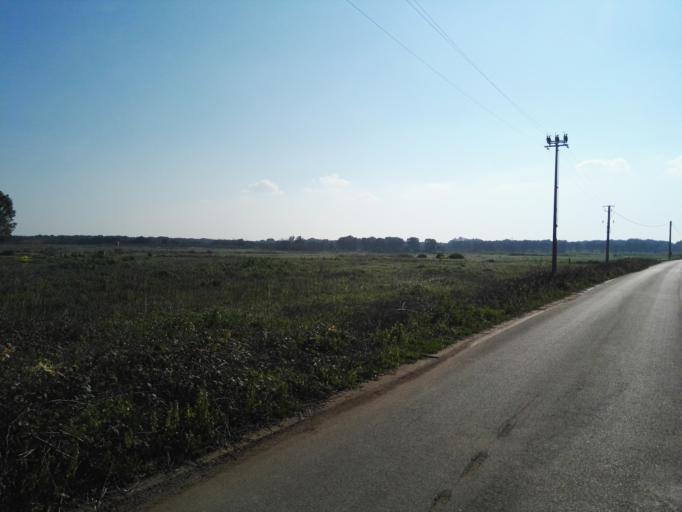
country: IT
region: Apulia
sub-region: Provincia di Brindisi
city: Torchiarolo
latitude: 40.5184
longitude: 18.0306
